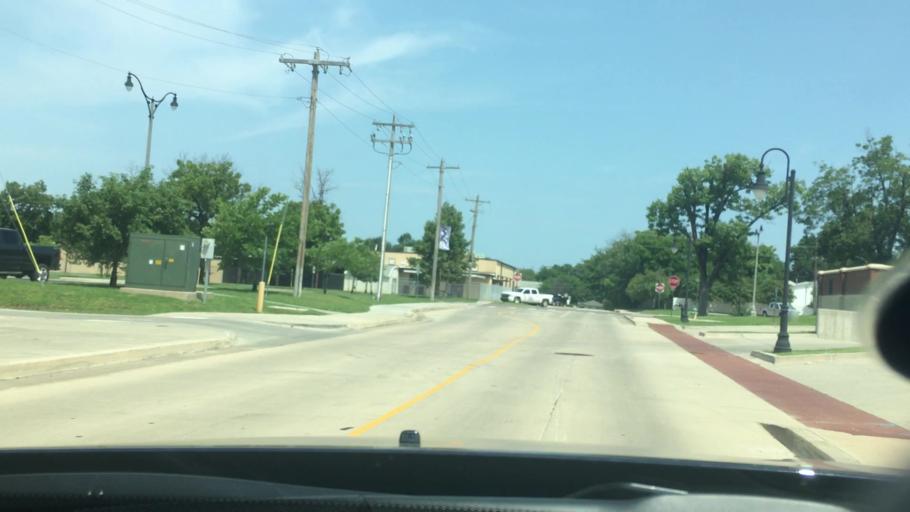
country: US
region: Oklahoma
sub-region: Pontotoc County
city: Ada
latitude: 34.7749
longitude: -96.6668
